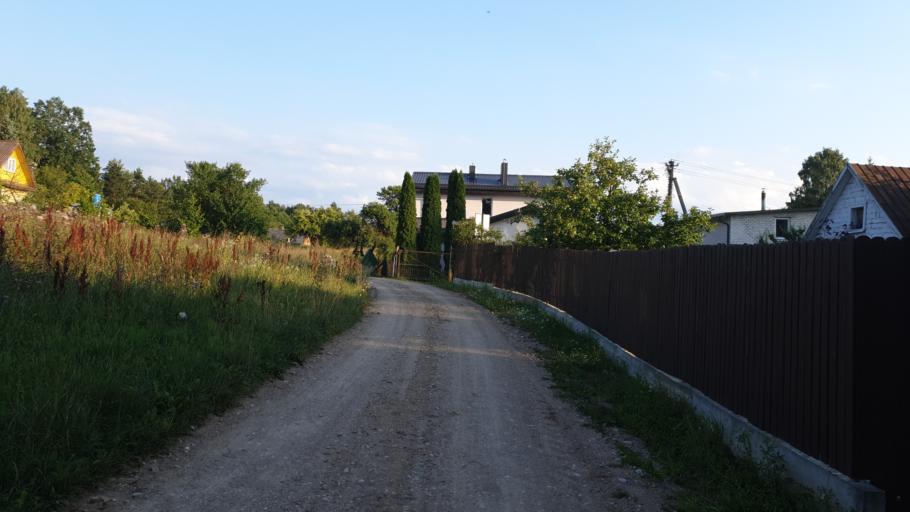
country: LT
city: Grigiskes
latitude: 54.7608
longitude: 25.0273
